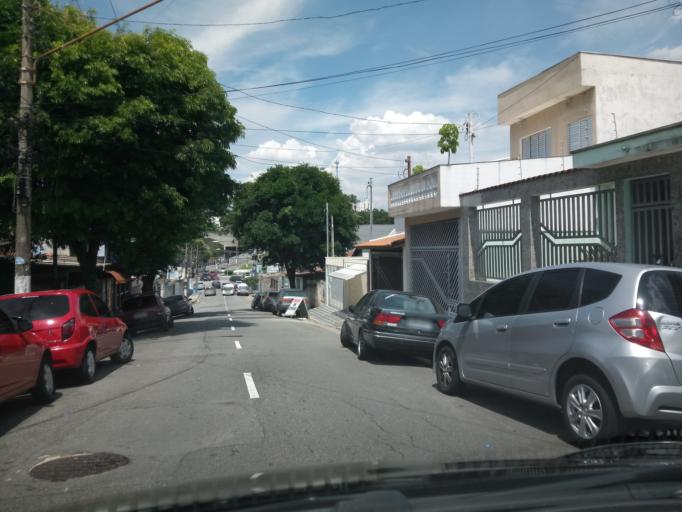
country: BR
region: Sao Paulo
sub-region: Sao Bernardo Do Campo
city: Sao Bernardo do Campo
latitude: -23.6979
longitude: -46.5793
